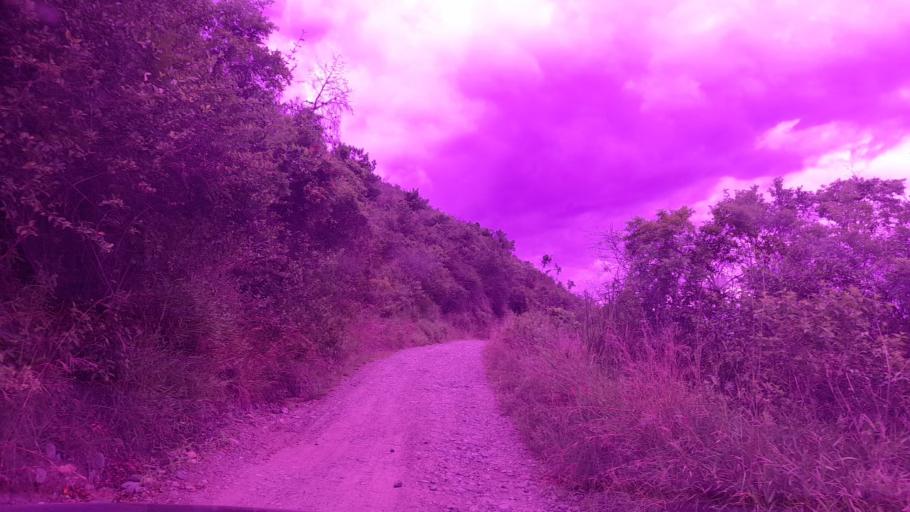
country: CO
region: Valle del Cauca
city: Andalucia
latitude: 4.1744
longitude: -76.1244
